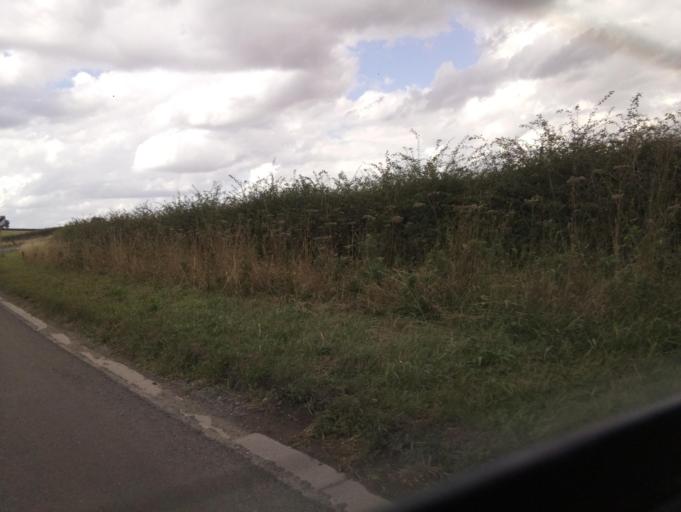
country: GB
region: England
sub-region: North Yorkshire
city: Ripon
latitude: 54.1548
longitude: -1.5388
